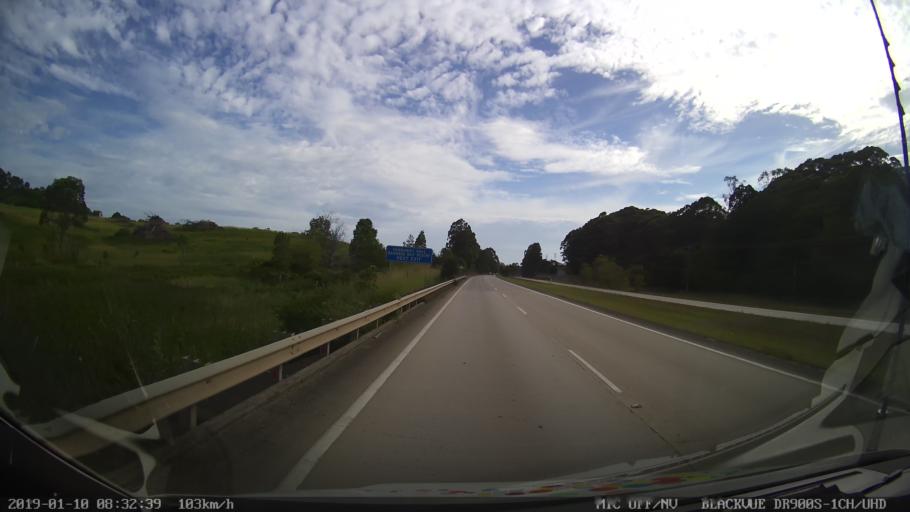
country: AU
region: New South Wales
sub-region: Coffs Harbour
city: Boambee
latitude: -30.3413
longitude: 153.0727
